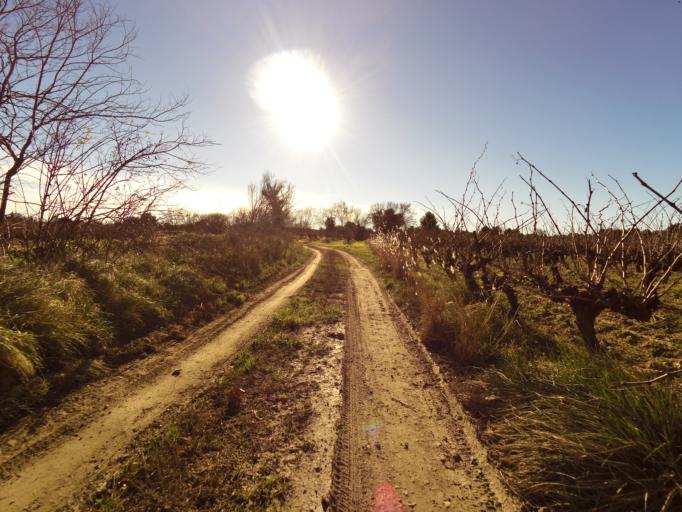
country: FR
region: Languedoc-Roussillon
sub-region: Departement du Gard
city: Gallargues-le-Montueux
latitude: 43.7305
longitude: 4.1583
